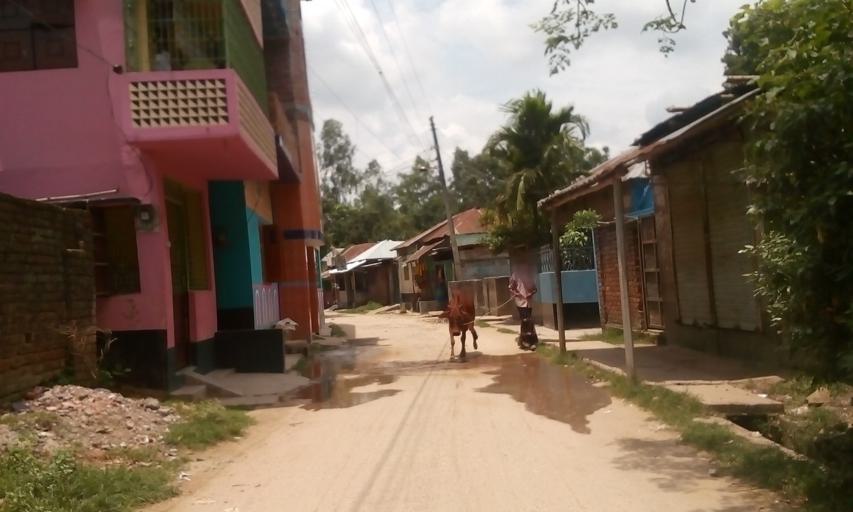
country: IN
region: West Bengal
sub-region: Dakshin Dinajpur
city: Balurghat
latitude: 25.3911
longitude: 88.9878
